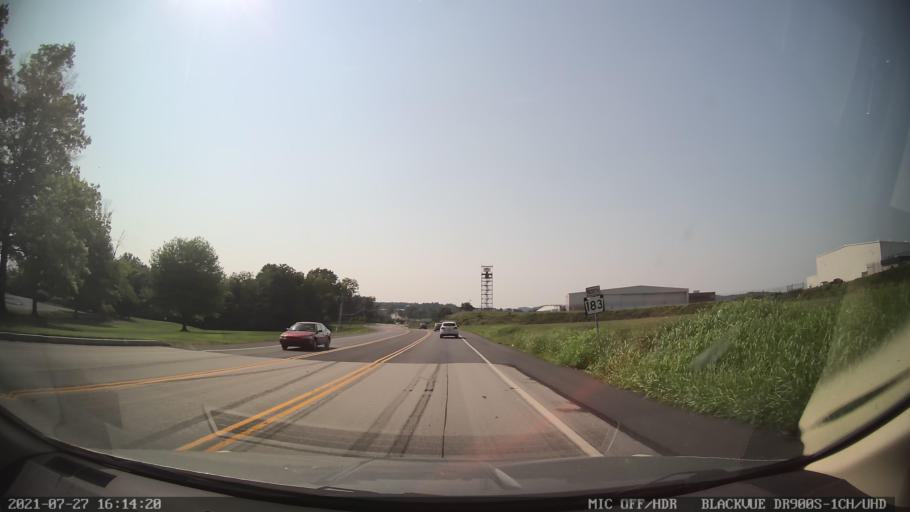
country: US
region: Pennsylvania
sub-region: Berks County
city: River View Park
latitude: 40.3731
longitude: -75.9675
